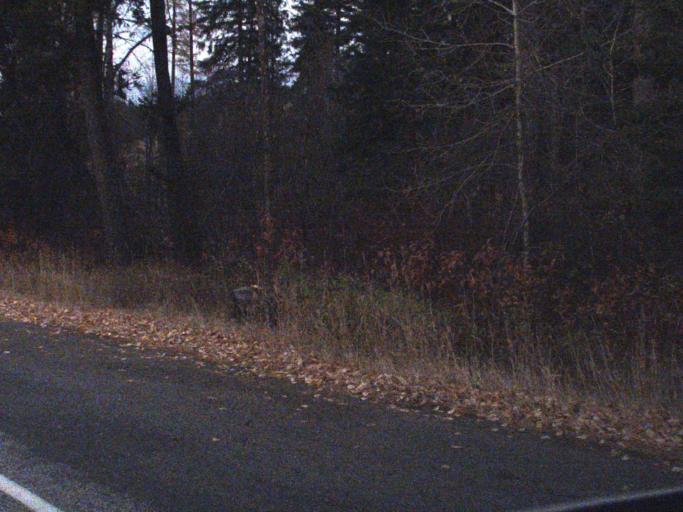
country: US
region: Washington
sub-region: Ferry County
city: Republic
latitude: 48.6020
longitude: -118.6545
